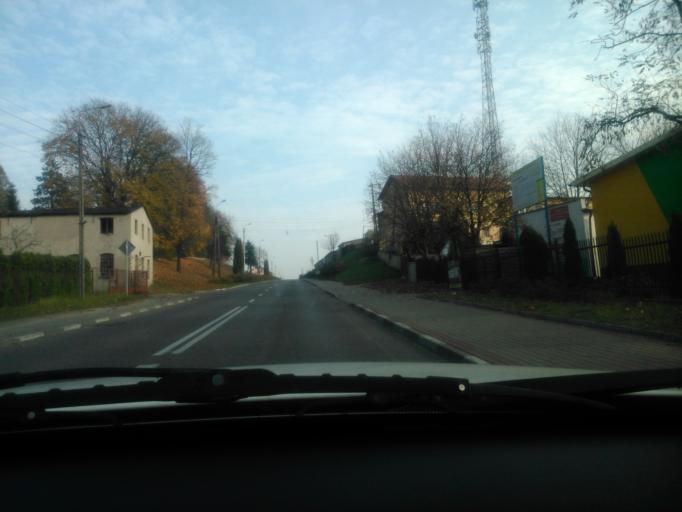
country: PL
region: Warmian-Masurian Voivodeship
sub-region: Powiat dzialdowski
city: Lidzbark
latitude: 53.2626
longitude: 19.8286
